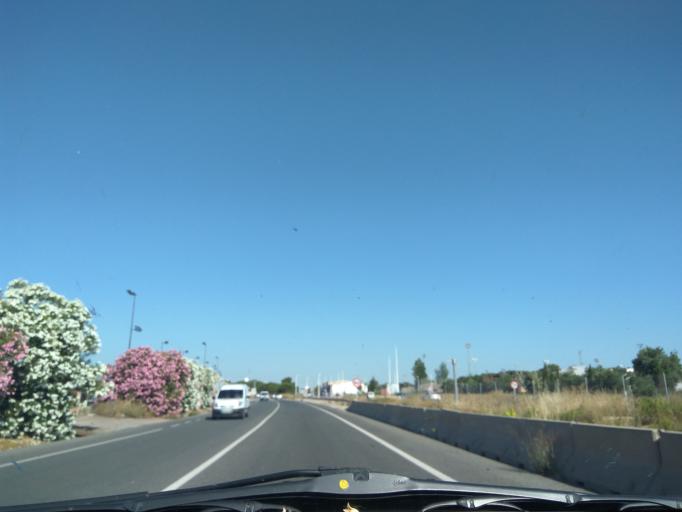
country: ES
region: Valencia
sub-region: Provincia de Valencia
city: Manises
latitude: 39.4952
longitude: -0.4748
